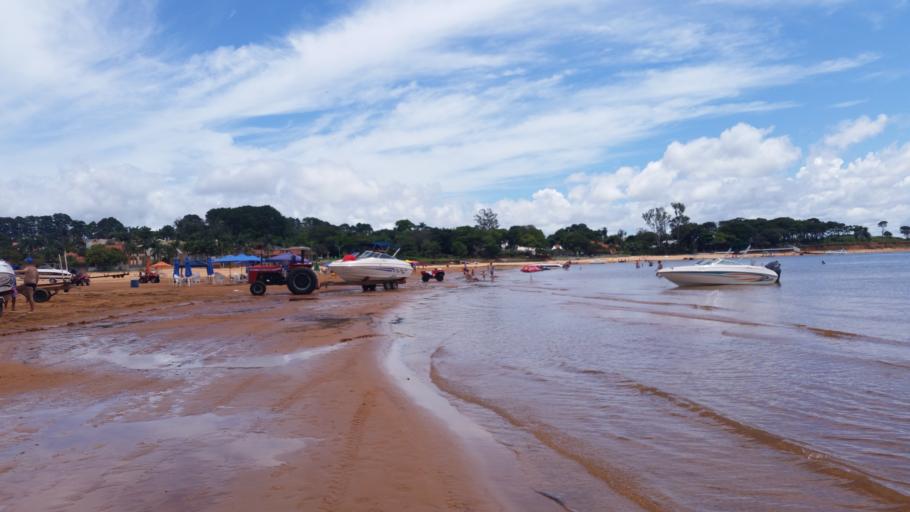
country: BR
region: Sao Paulo
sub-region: Itai
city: Itai
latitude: -23.2810
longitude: -49.0195
